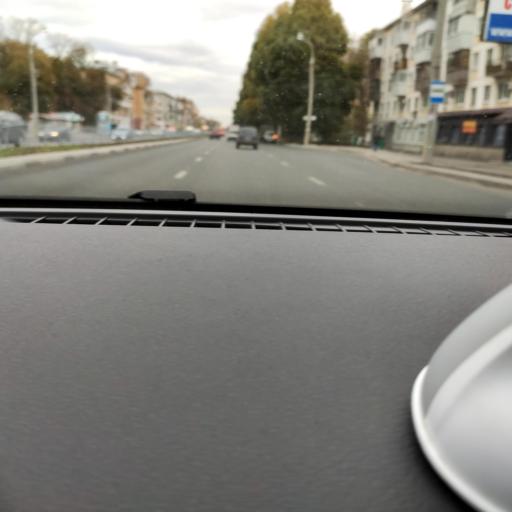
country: RU
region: Samara
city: Samara
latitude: 53.2036
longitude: 50.2283
